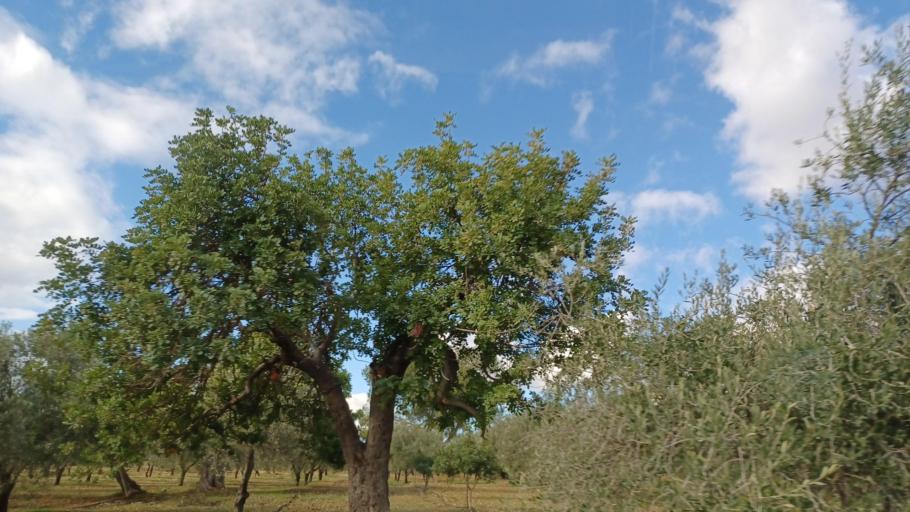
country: CY
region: Limassol
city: Sotira
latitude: 34.7445
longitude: 32.8576
